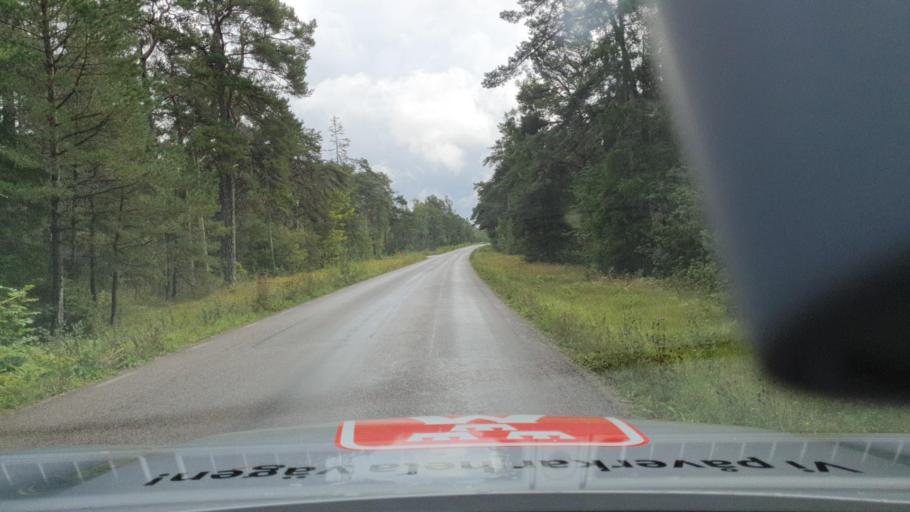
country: SE
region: Gotland
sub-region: Gotland
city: Slite
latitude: 57.7266
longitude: 18.7490
